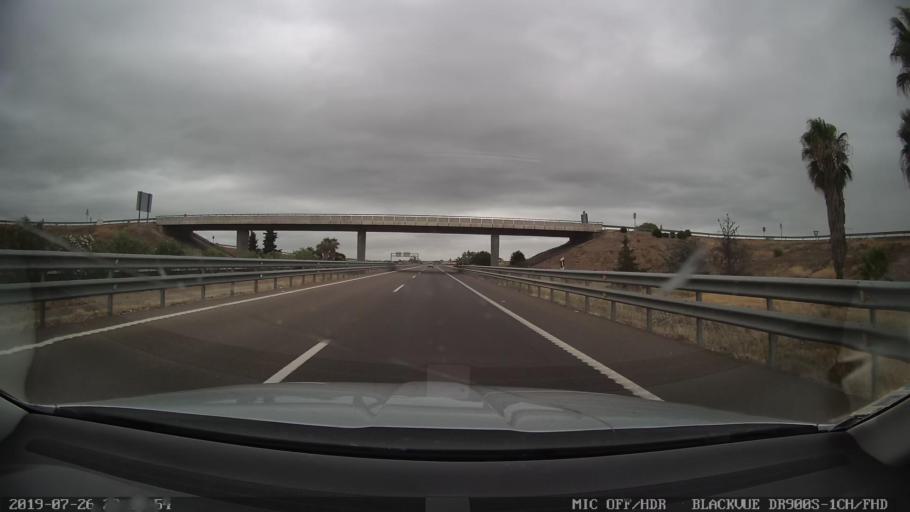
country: ES
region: Extremadura
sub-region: Provincia de Badajoz
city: San Pedro de Merida
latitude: 38.9897
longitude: -6.1222
